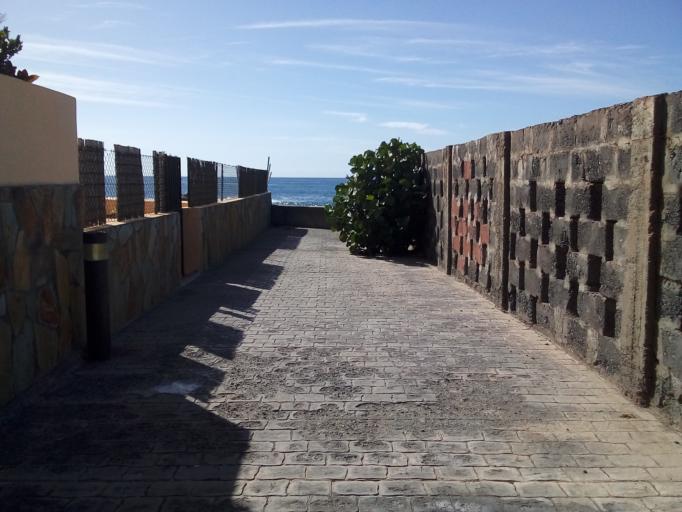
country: ES
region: Canary Islands
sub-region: Provincia de Santa Cruz de Tenerife
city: Alajero
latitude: 28.0959
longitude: -17.3445
